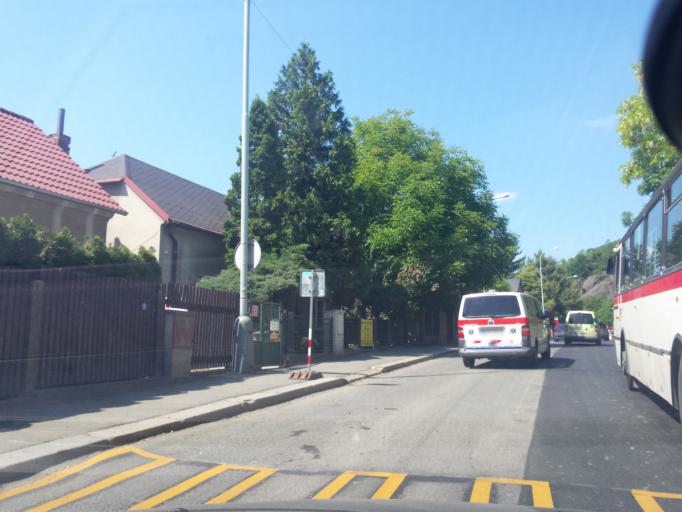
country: CZ
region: Central Bohemia
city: Horomerice
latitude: 50.1066
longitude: 14.3533
